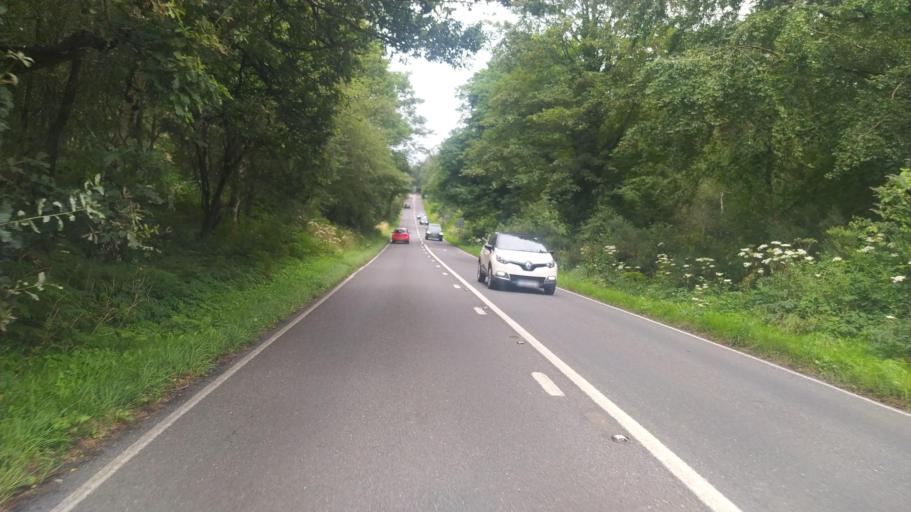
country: GB
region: England
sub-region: Hampshire
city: Liphook
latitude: 51.0608
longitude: -0.8127
